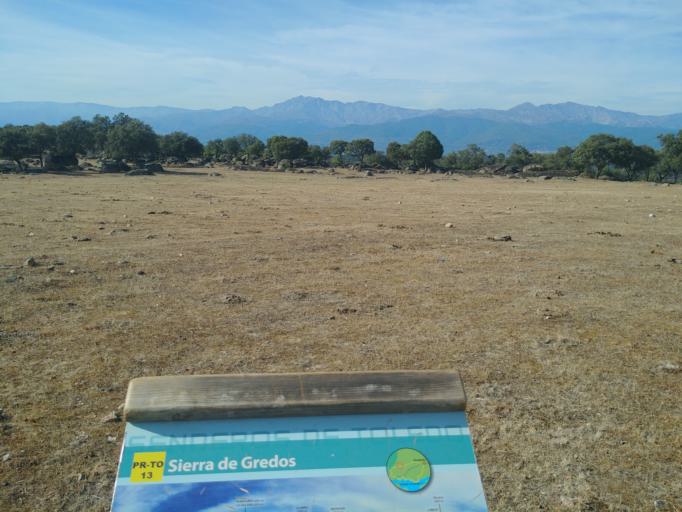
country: ES
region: Castille-La Mancha
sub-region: Province of Toledo
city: Navalcan
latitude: 40.0638
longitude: -5.1336
